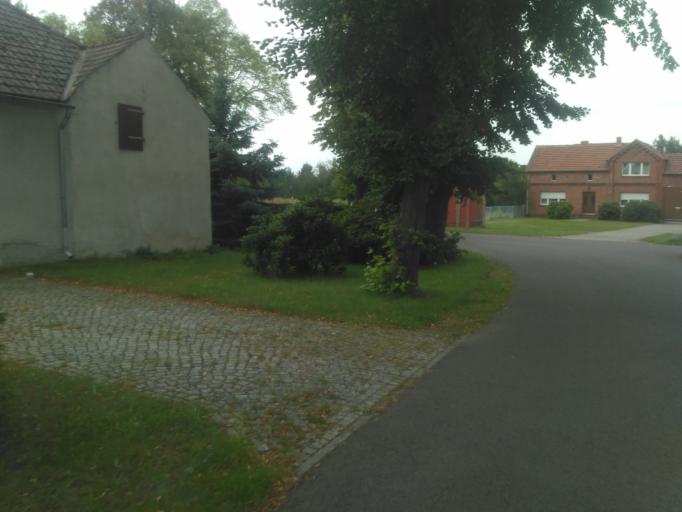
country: DE
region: Brandenburg
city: Welzow
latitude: 51.5172
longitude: 14.1886
